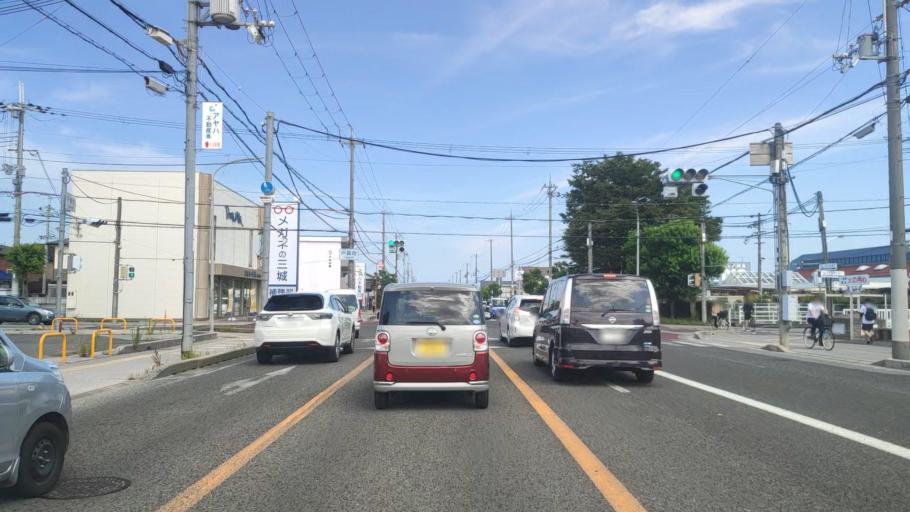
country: JP
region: Shiga Prefecture
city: Hikone
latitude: 35.2538
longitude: 136.2402
